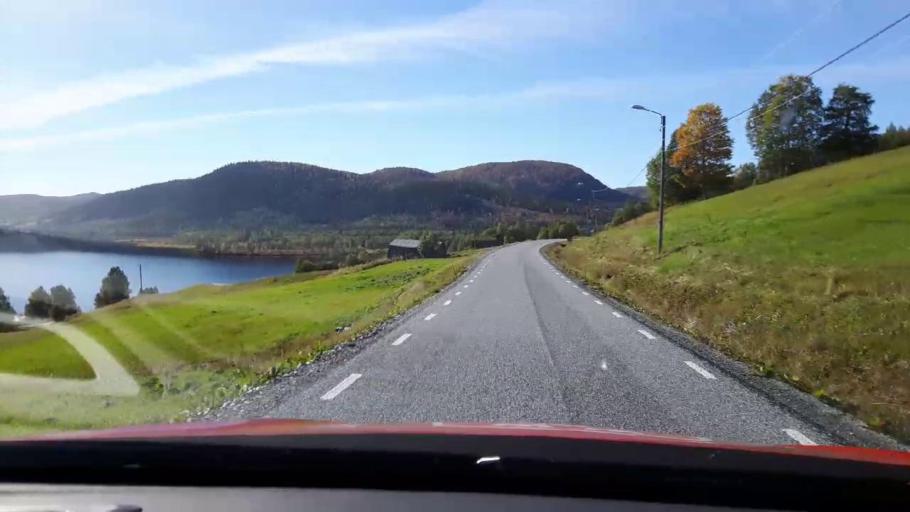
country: NO
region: Nord-Trondelag
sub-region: Royrvik
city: Royrvik
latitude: 64.7287
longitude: 13.9799
